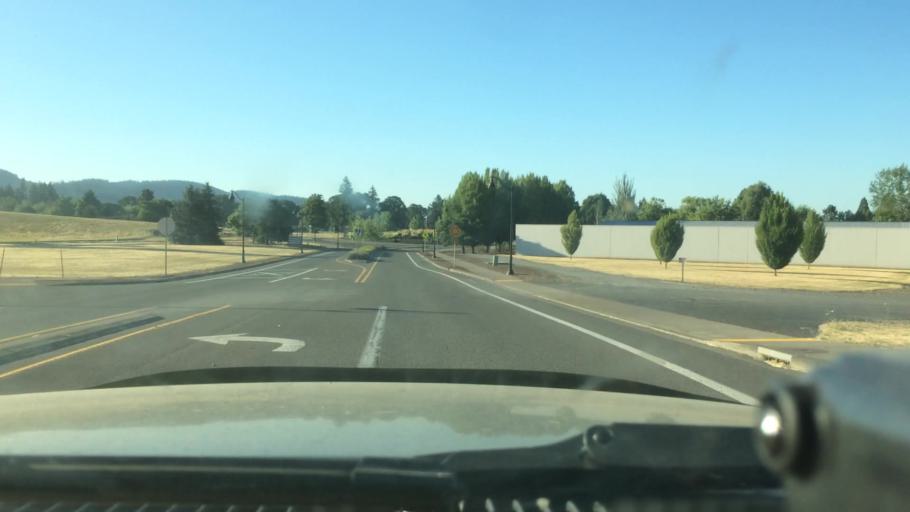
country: US
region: Oregon
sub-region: Yamhill County
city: Newberg
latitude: 45.3169
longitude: -122.9473
